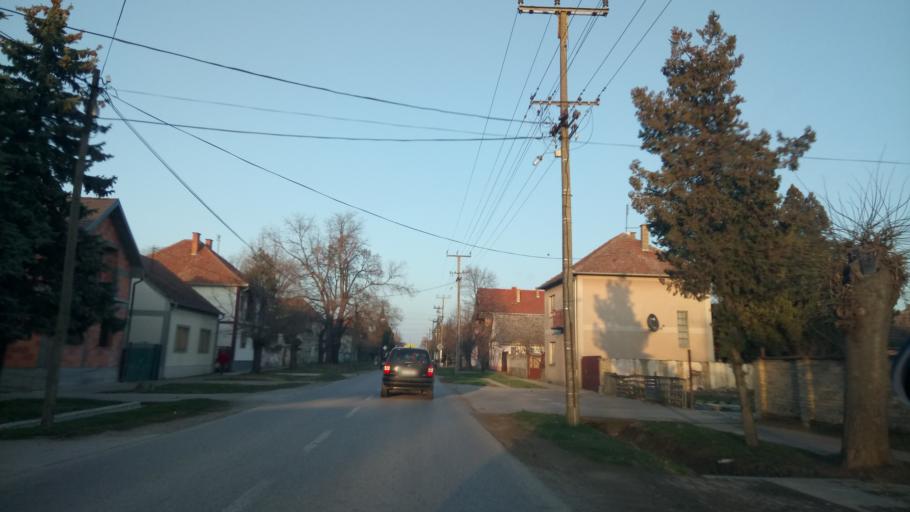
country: RS
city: Novi Slankamen
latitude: 45.1209
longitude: 20.2327
